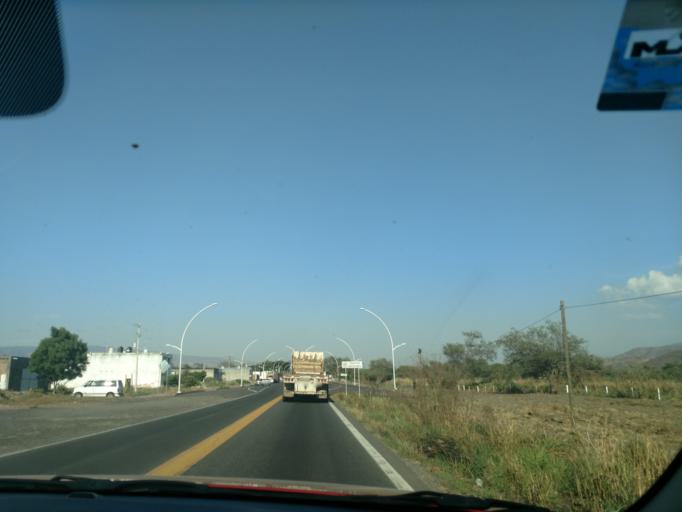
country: MX
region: Nayarit
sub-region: Ahuacatlan
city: Ahuacatlan
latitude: 21.0589
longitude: -104.4956
